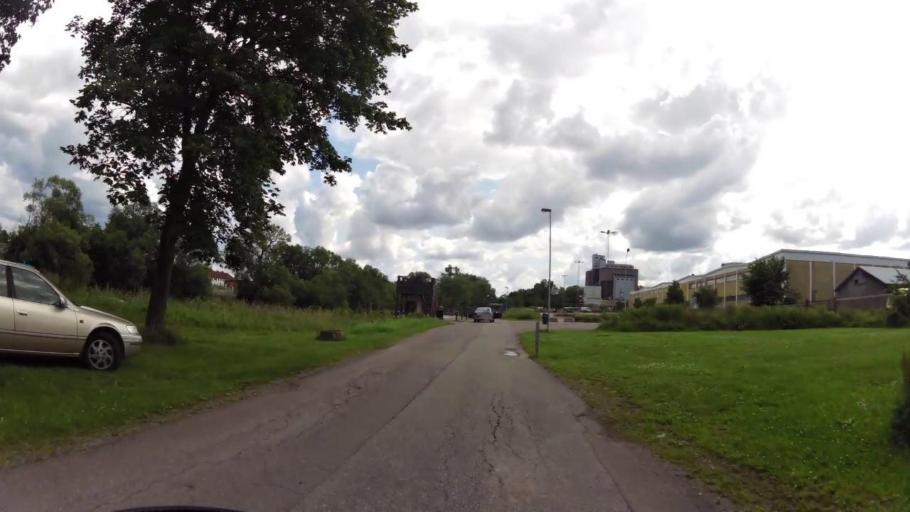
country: SE
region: OEstergoetland
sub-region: Linkopings Kommun
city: Linkoping
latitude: 58.4250
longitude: 15.6290
